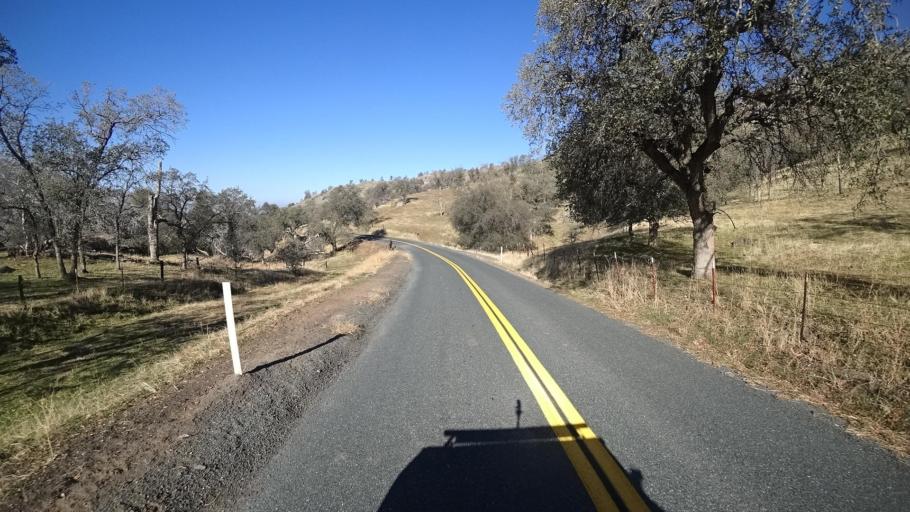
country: US
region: California
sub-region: Kern County
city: Alta Sierra
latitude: 35.7886
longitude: -118.7922
